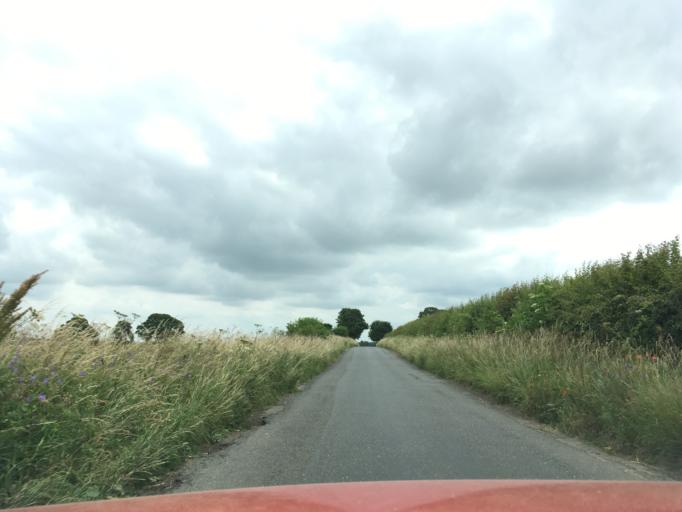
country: GB
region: England
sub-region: Oxfordshire
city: Charlbury
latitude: 51.9174
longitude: -1.4784
